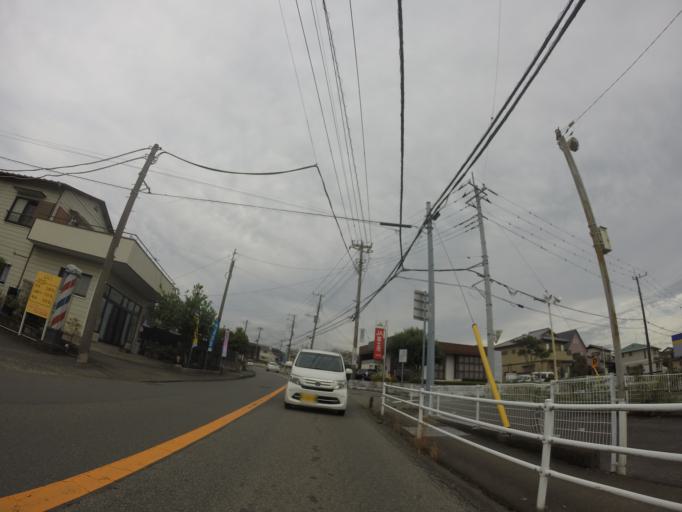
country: JP
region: Shizuoka
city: Fuji
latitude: 35.1872
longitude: 138.6651
